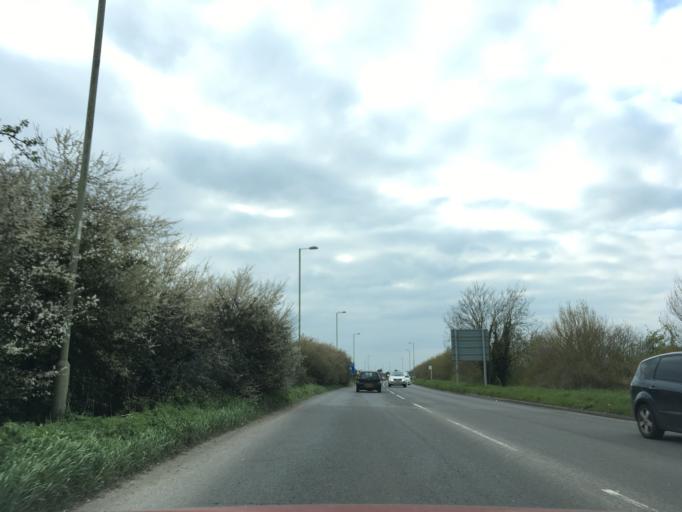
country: GB
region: England
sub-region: Oxfordshire
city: Witney
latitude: 51.7916
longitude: -1.5118
